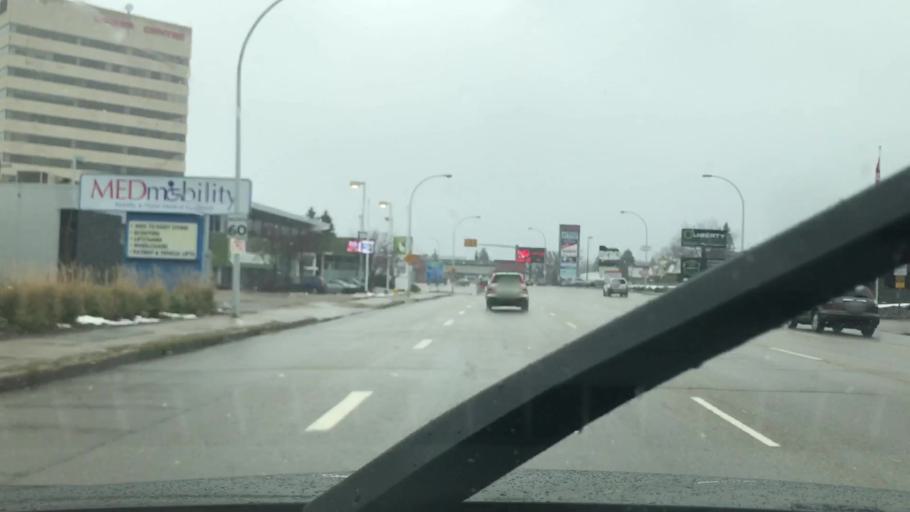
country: CA
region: Alberta
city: Edmonton
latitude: 53.4945
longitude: -113.4976
